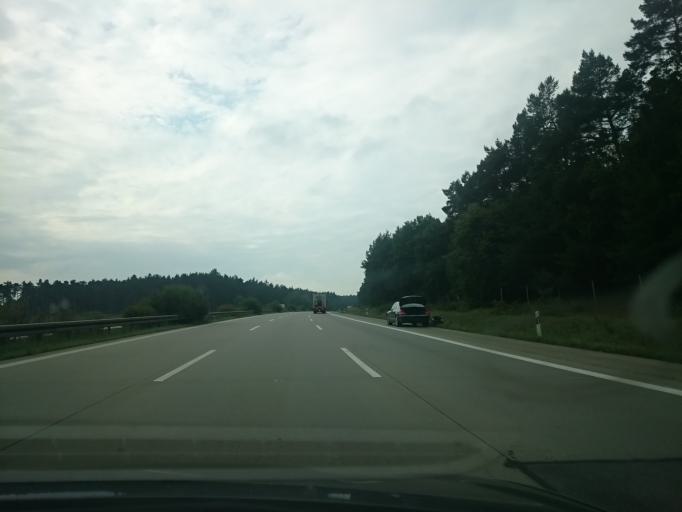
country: DE
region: Brandenburg
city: Niemegk
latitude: 52.0523
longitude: 12.6462
